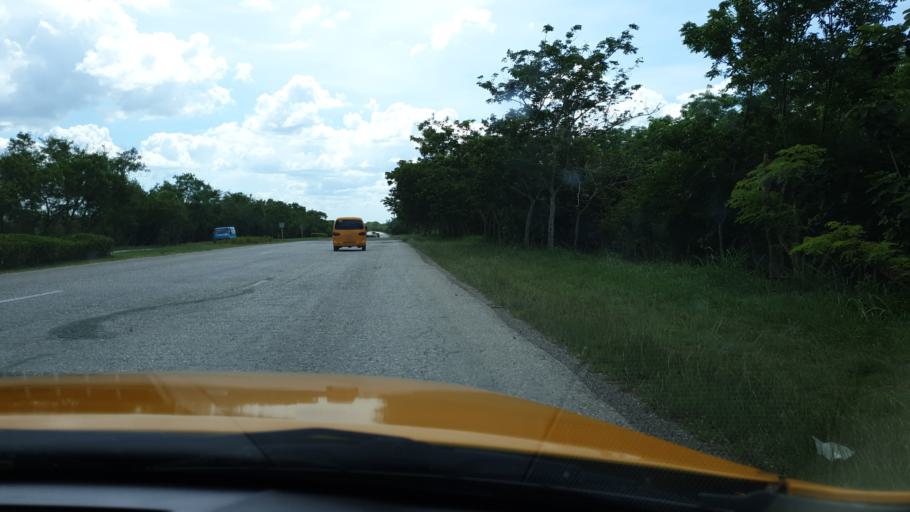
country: CU
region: Cienfuegos
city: Cruces
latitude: 22.4536
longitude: -80.2944
